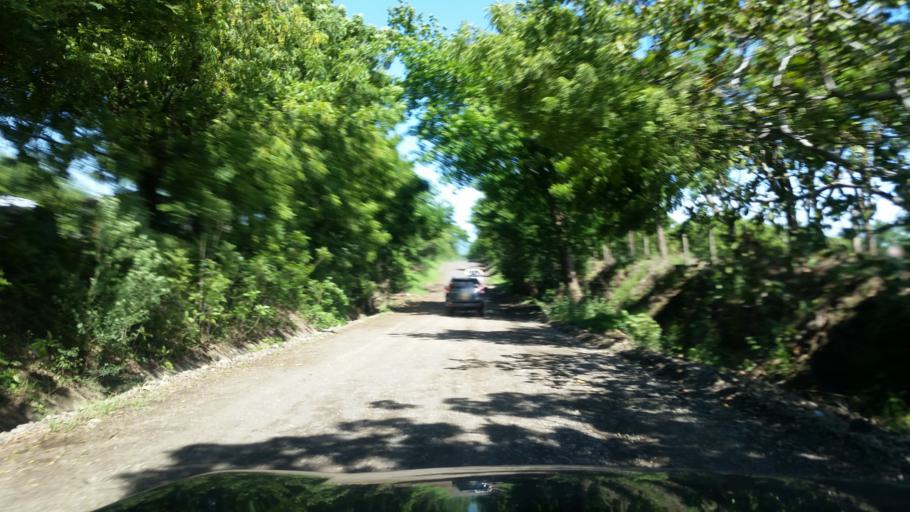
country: NI
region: Chinandega
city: Puerto Morazan
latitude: 12.7697
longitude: -87.0774
